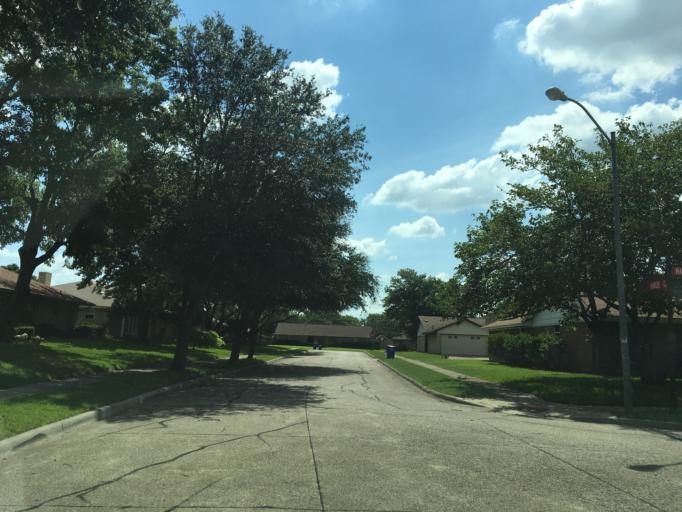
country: US
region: Texas
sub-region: Dallas County
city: Farmers Branch
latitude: 32.9266
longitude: -96.8750
